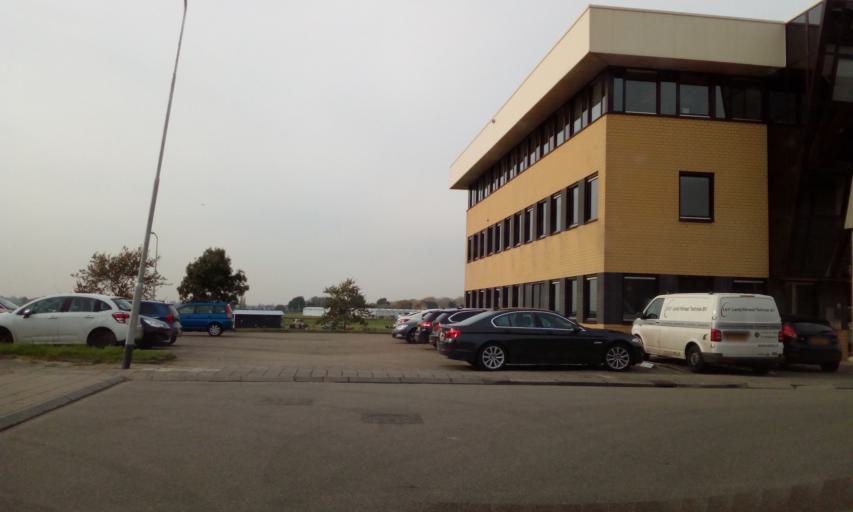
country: NL
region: South Holland
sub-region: Gemeente Lansingerland
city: Berkel en Rodenrijs
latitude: 51.9729
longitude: 4.4609
